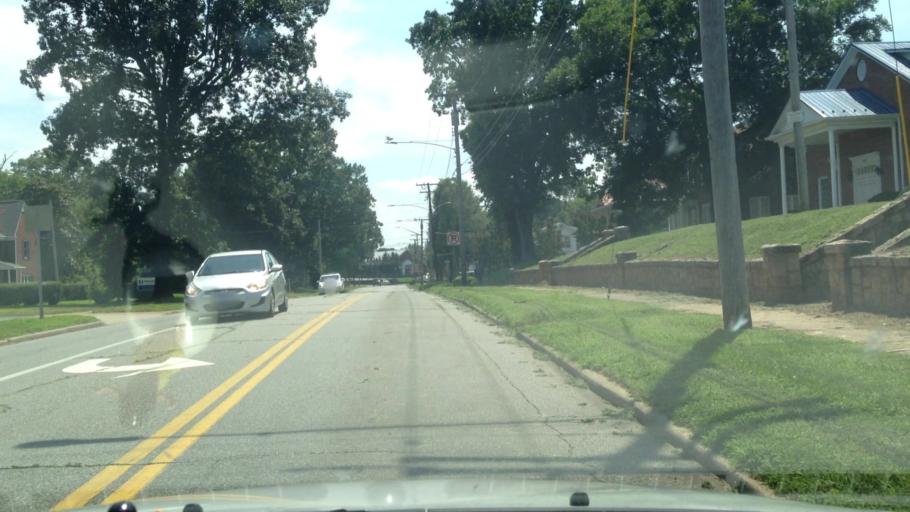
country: US
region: Virginia
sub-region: City of Martinsville
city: Martinsville
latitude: 36.6810
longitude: -79.8705
